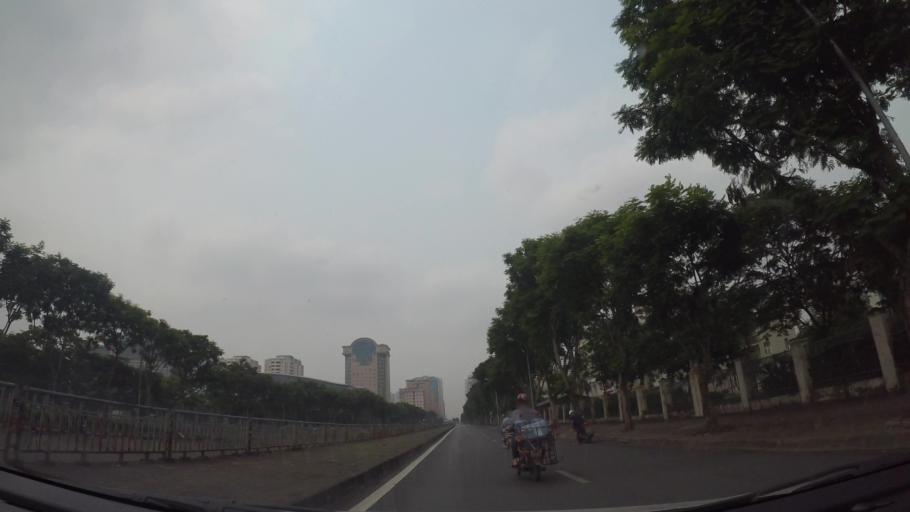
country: VN
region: Ha Noi
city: Cau Dien
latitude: 21.0263
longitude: 105.7632
